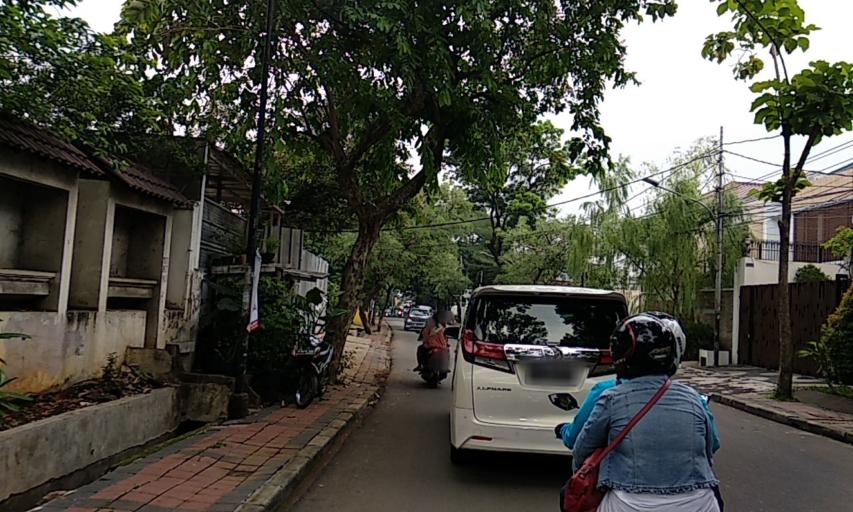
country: ID
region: Jakarta Raya
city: Jakarta
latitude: -6.2397
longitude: 106.8563
